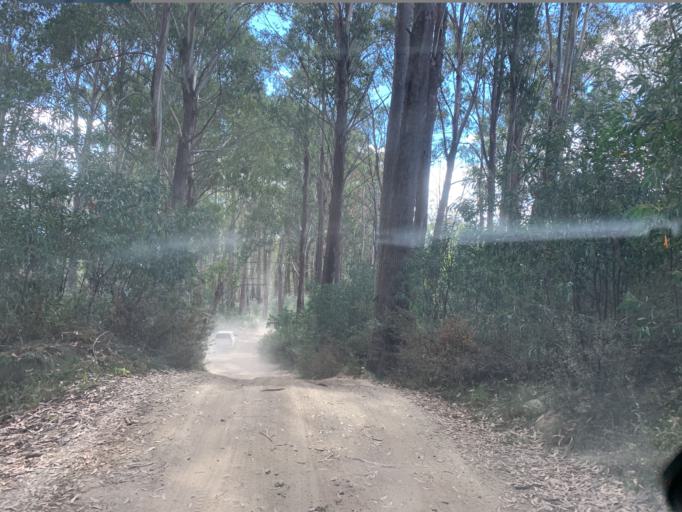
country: AU
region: Victoria
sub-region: Mansfield
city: Mansfield
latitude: -37.0996
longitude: 146.5449
